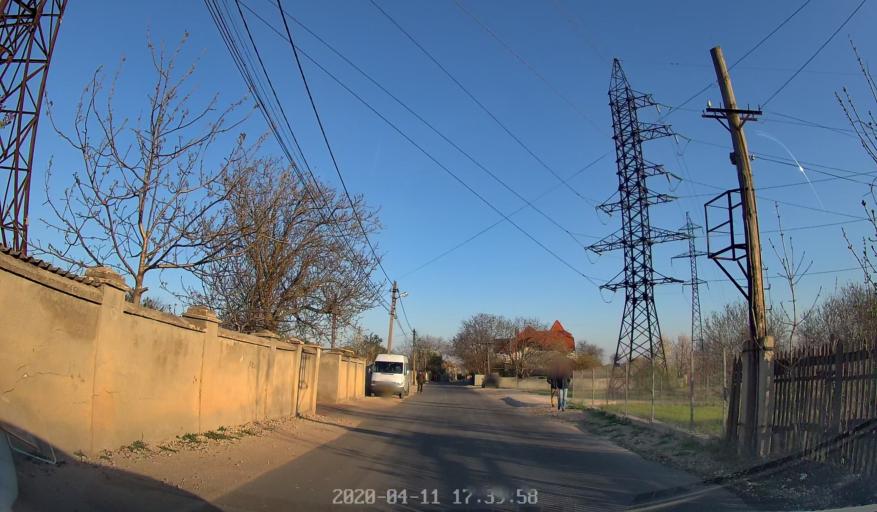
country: MD
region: Laloveni
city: Ialoveni
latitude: 46.9814
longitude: 28.8086
